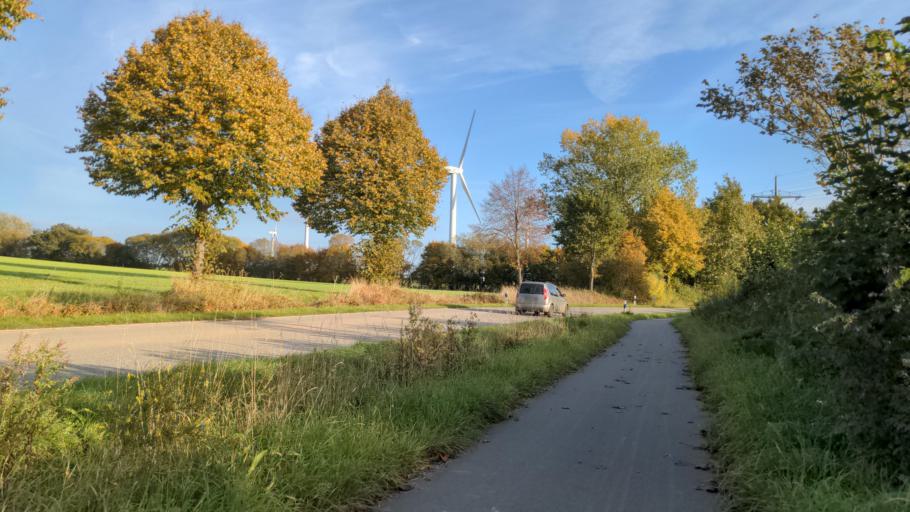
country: DE
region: Schleswig-Holstein
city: Manhagen
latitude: 54.2083
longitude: 10.9240
